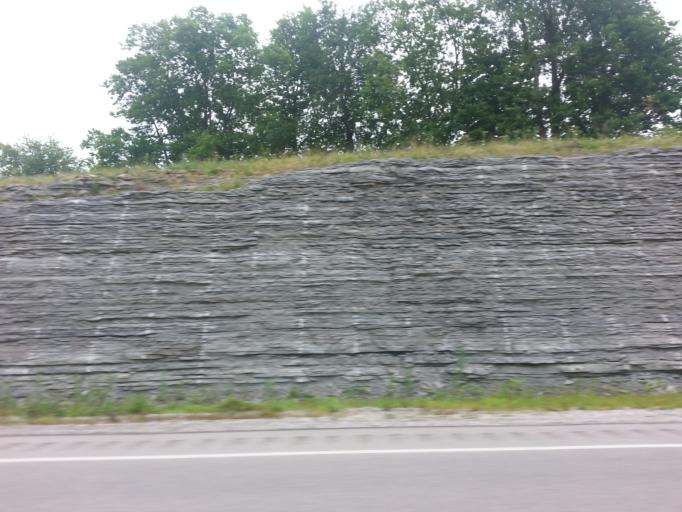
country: US
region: Ohio
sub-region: Brown County
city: Aberdeen
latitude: 38.5951
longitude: -83.8190
